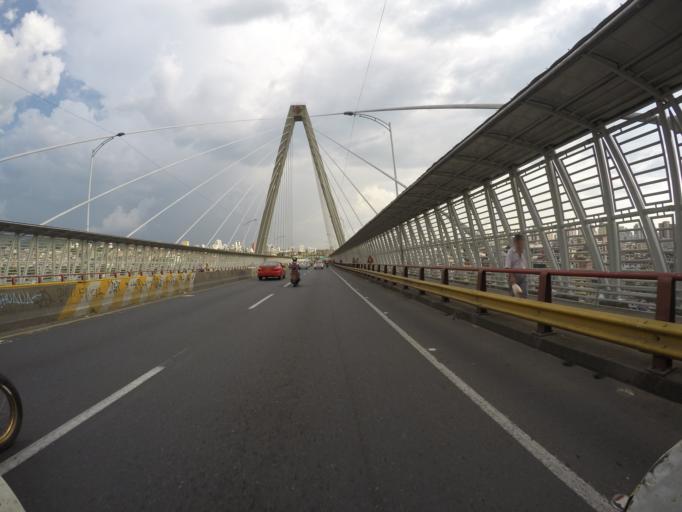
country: CO
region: Risaralda
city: Pereira
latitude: 4.8162
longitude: -75.6872
